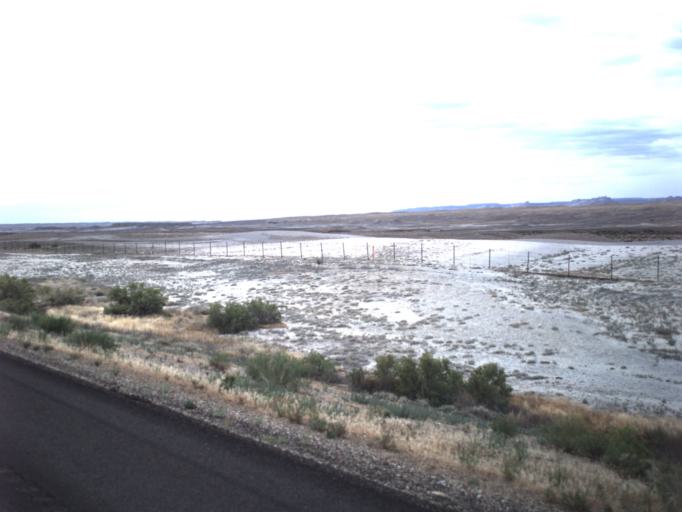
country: US
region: Utah
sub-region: Carbon County
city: East Carbon City
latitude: 39.0608
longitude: -110.3129
